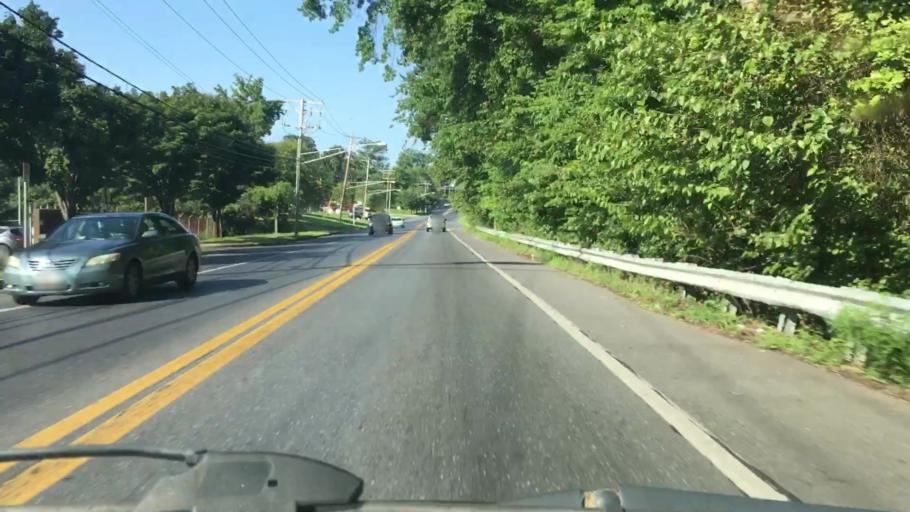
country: US
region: Maryland
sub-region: Prince George's County
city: Seabrook
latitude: 38.9768
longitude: -76.8384
